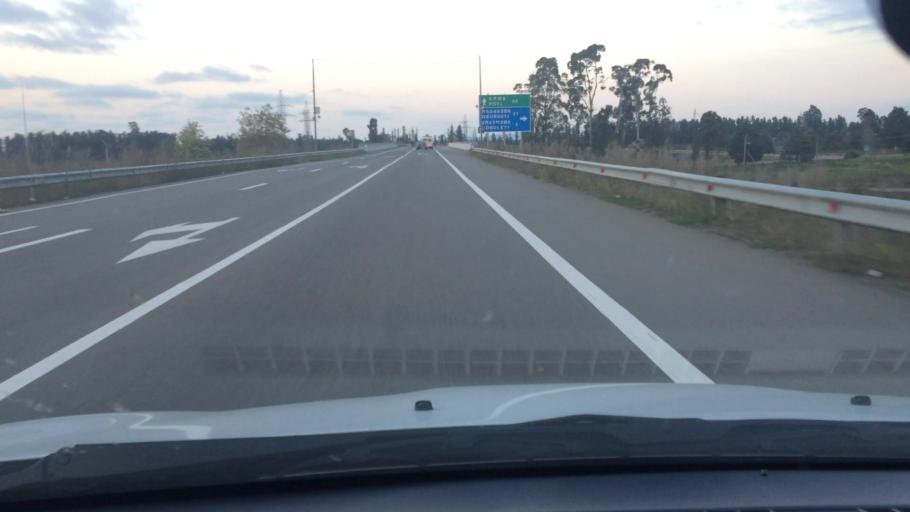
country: GE
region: Ajaria
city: Ochkhamuri
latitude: 41.8294
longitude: 41.8200
